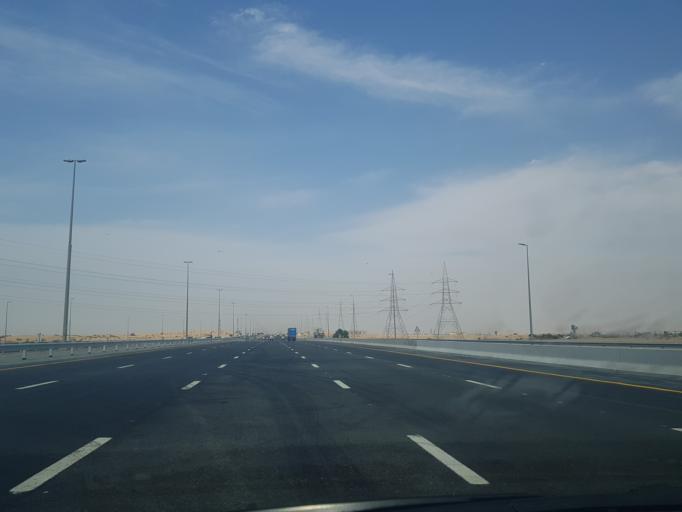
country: AE
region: Ash Shariqah
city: Sharjah
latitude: 25.2417
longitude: 55.5682
